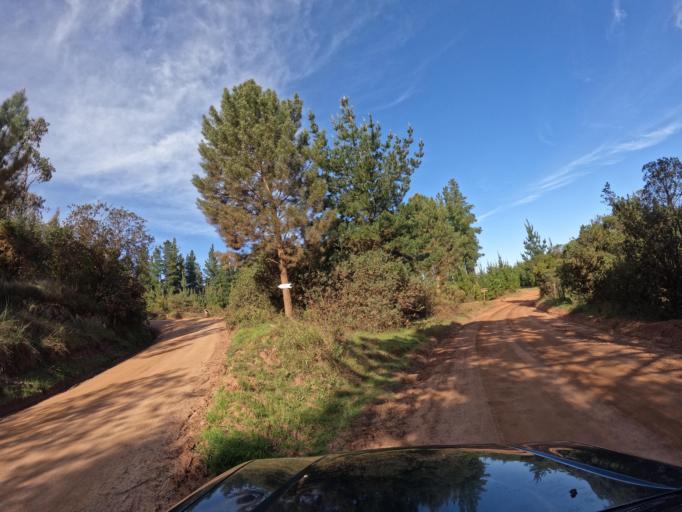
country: CL
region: Biobio
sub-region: Provincia de Biobio
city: Yumbel
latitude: -37.1002
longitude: -72.7413
